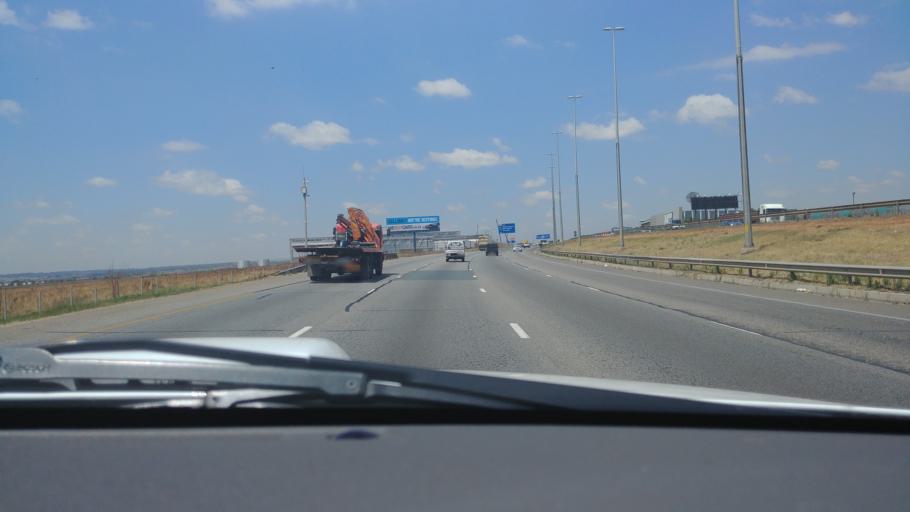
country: ZA
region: Gauteng
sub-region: Ekurhuleni Metropolitan Municipality
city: Tembisa
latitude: -26.0178
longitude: 28.2595
